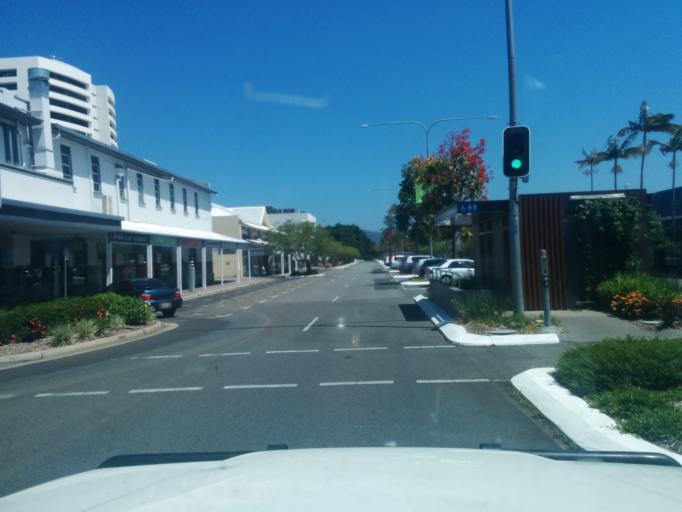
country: AU
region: Queensland
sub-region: Cairns
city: Cairns
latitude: -16.9246
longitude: 145.7763
